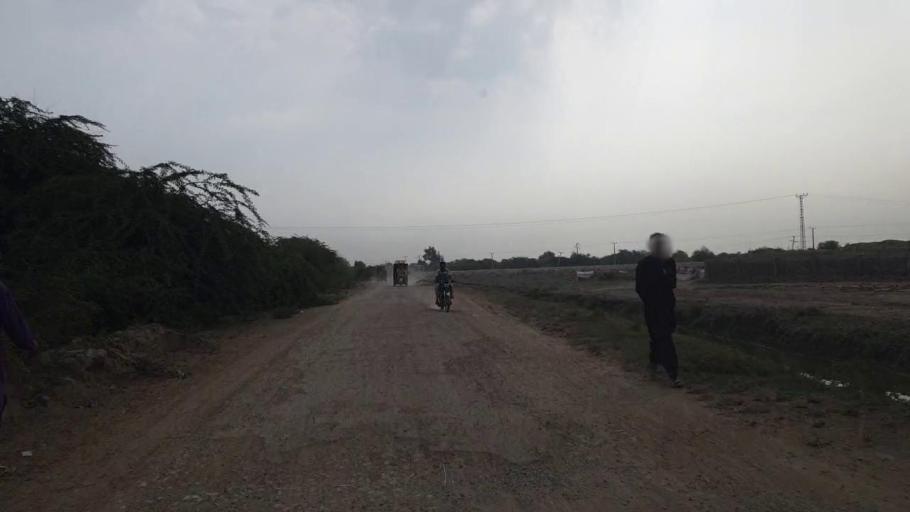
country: PK
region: Sindh
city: Talhar
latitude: 24.8997
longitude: 68.7735
